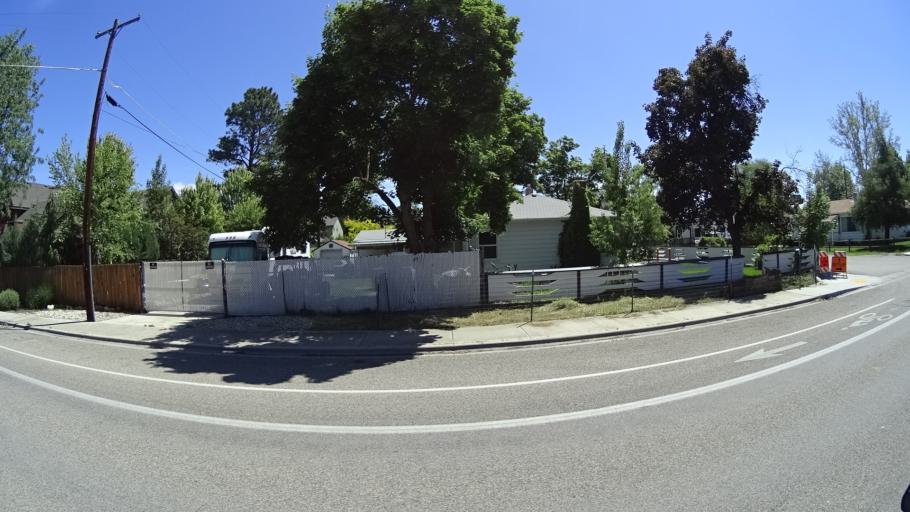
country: US
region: Idaho
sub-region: Ada County
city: Boise
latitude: 43.5825
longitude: -116.1836
